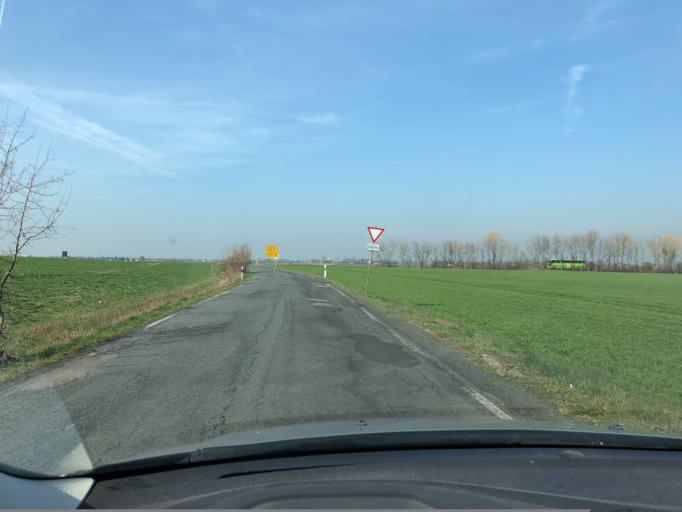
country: DE
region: Saxony
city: Rackwitz
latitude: 51.4249
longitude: 12.4068
